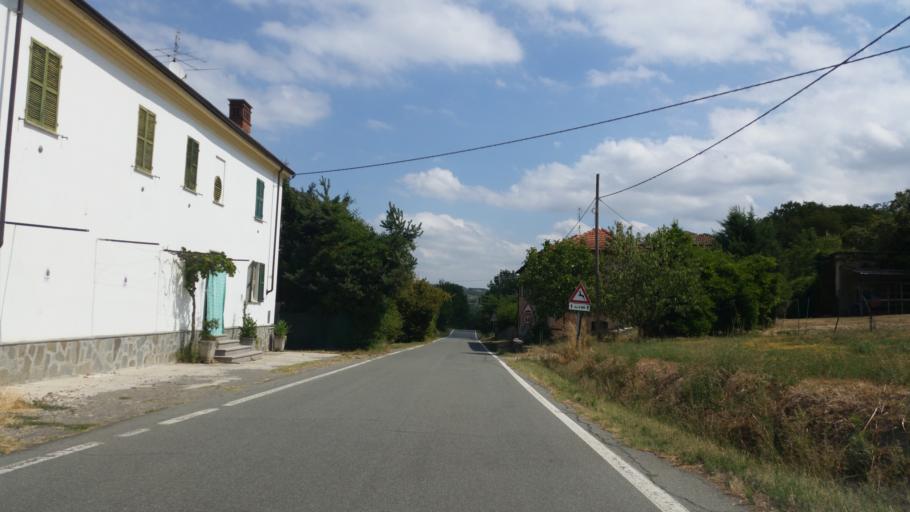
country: IT
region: Piedmont
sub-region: Provincia di Alessandria
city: Bistagno
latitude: 44.6523
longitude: 8.3649
